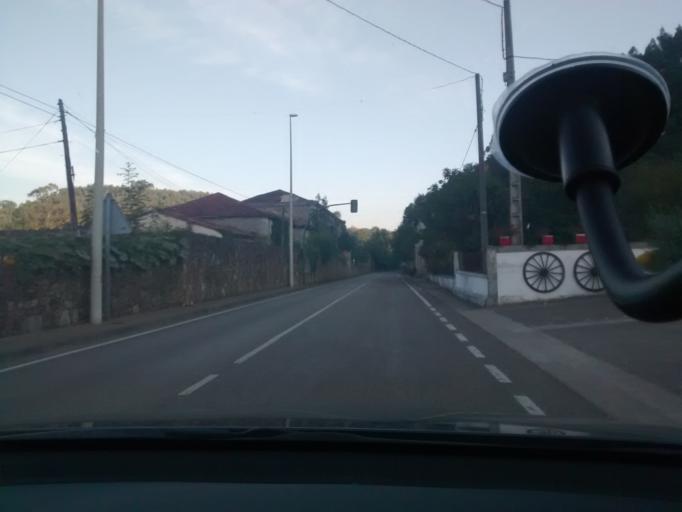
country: ES
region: Cantabria
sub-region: Provincia de Cantabria
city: Entrambasaguas
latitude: 43.3600
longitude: -3.7115
